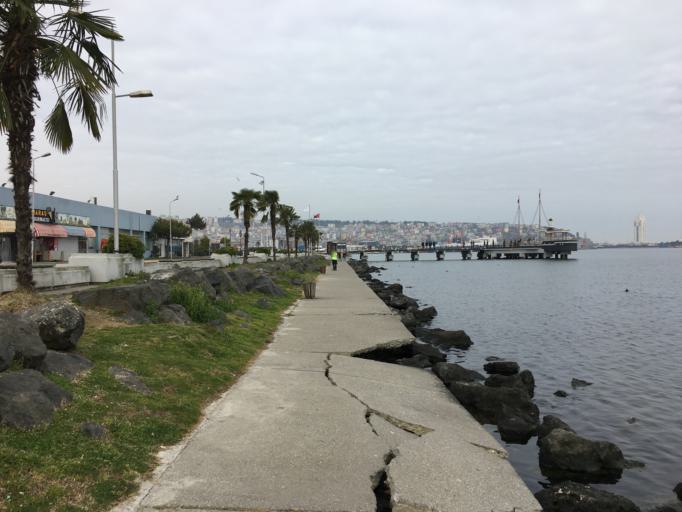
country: TR
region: Samsun
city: Samsun
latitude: 41.2918
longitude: 36.3410
